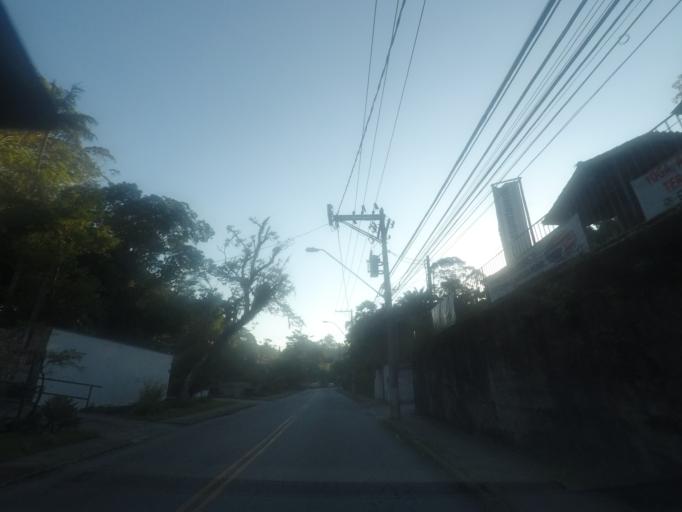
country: BR
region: Rio de Janeiro
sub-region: Petropolis
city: Petropolis
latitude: -22.5266
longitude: -43.1877
